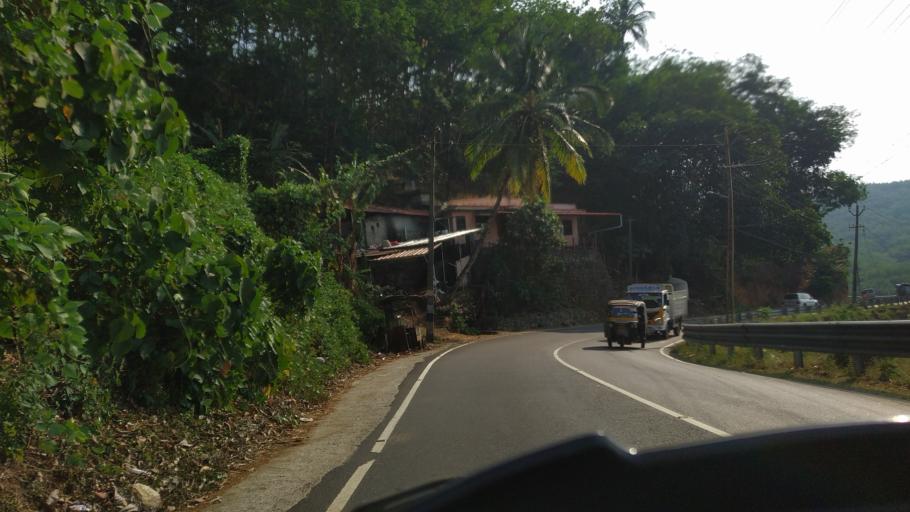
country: IN
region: Kerala
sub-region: Kottayam
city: Erattupetta
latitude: 9.5547
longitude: 76.9166
